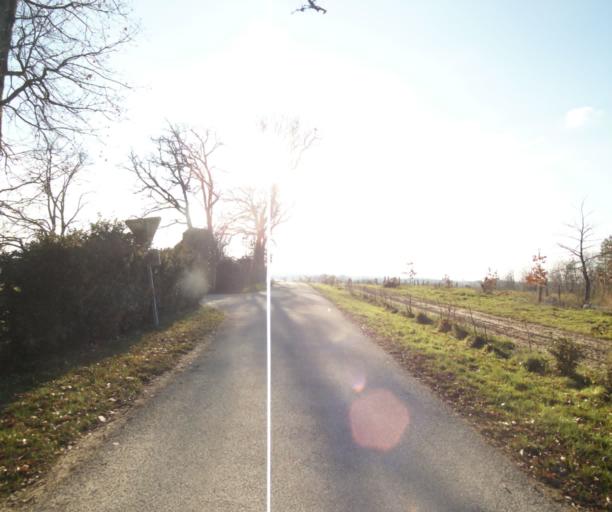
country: FR
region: Midi-Pyrenees
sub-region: Departement du Tarn-et-Garonne
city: Moissac
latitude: 44.1419
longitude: 1.0549
